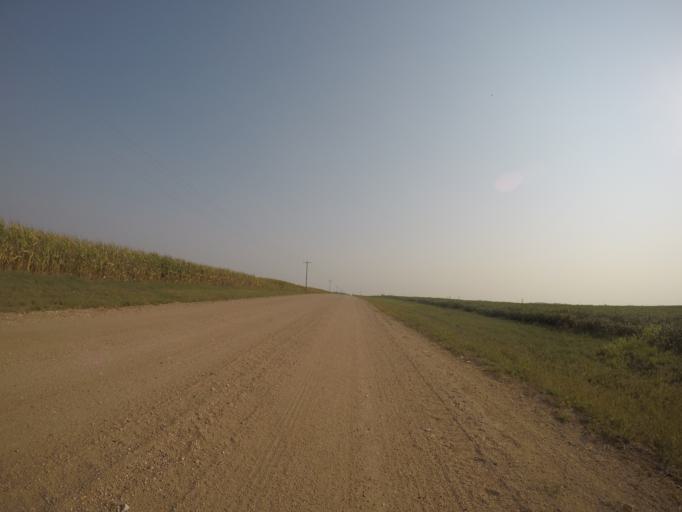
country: US
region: Nebraska
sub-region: Gage County
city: Beatrice
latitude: 40.2837
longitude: -96.8224
